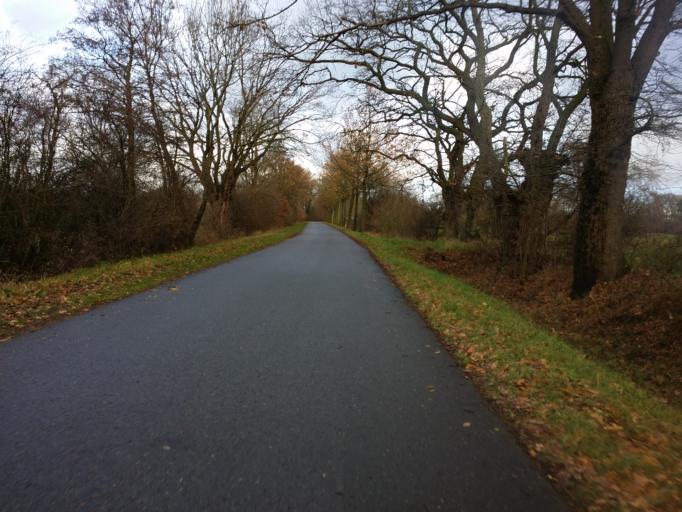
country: DE
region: Lower Saxony
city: Thedinghausen
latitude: 52.9731
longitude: 8.9894
